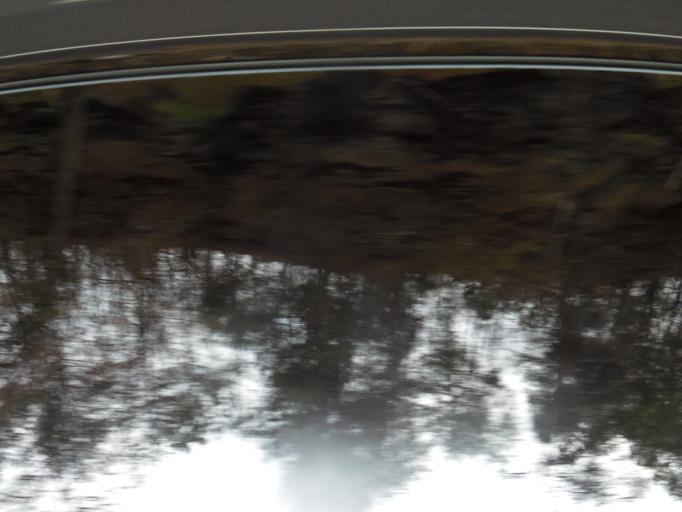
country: US
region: Alabama
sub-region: Blount County
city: Smoke Rise
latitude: 33.9073
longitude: -86.8642
